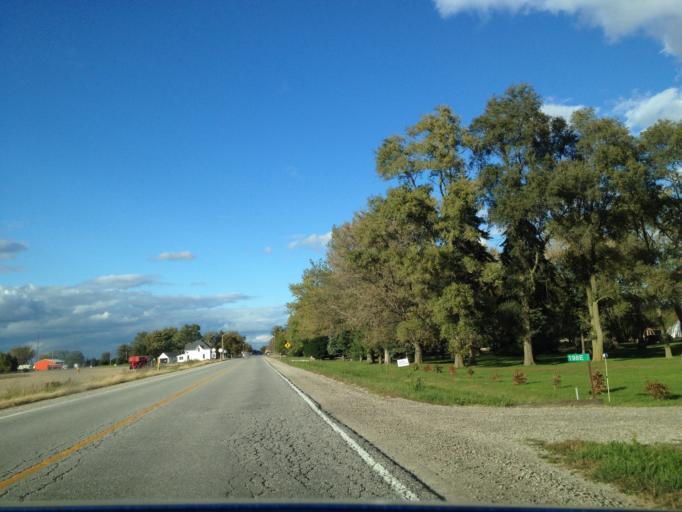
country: US
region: Michigan
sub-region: Wayne County
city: Grosse Pointe
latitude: 42.1359
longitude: -82.7337
